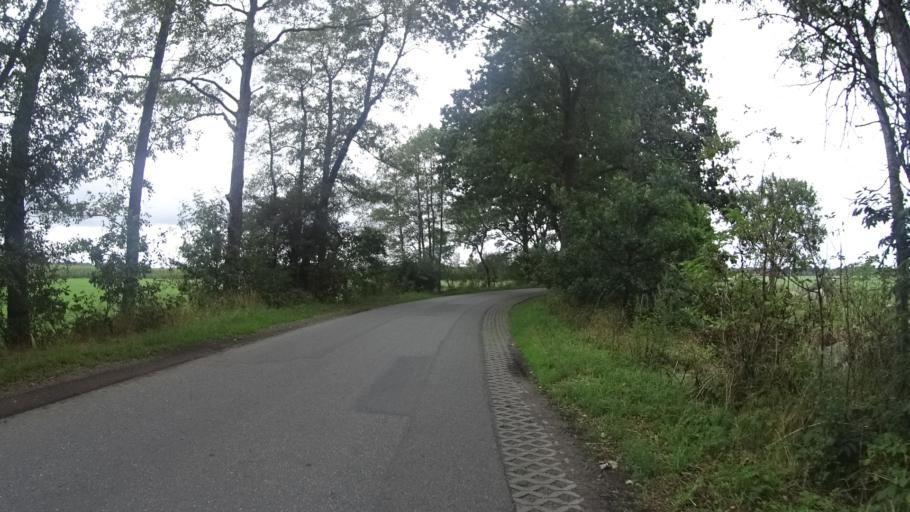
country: DE
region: Lower Saxony
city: Stinstedt
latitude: 53.6423
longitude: 8.9584
